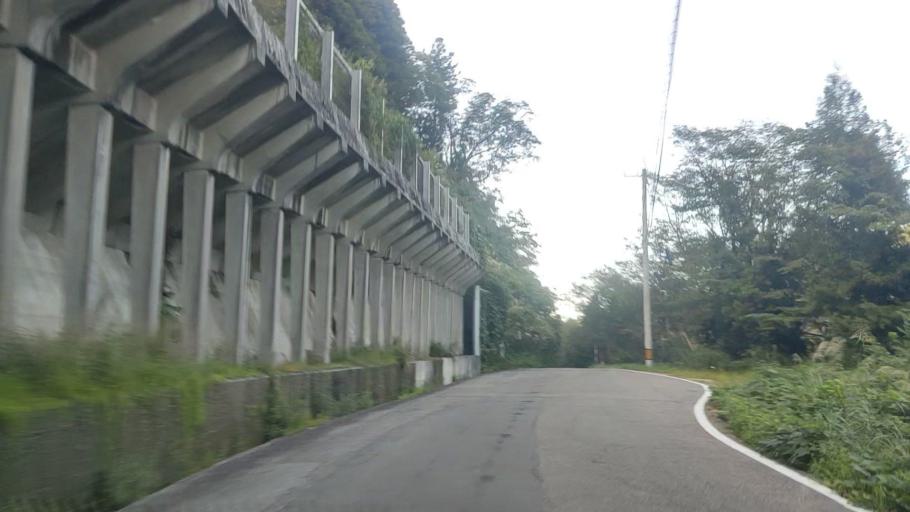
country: JP
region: Toyama
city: Yatsuomachi-higashikumisaka
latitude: 36.4933
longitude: 137.0625
